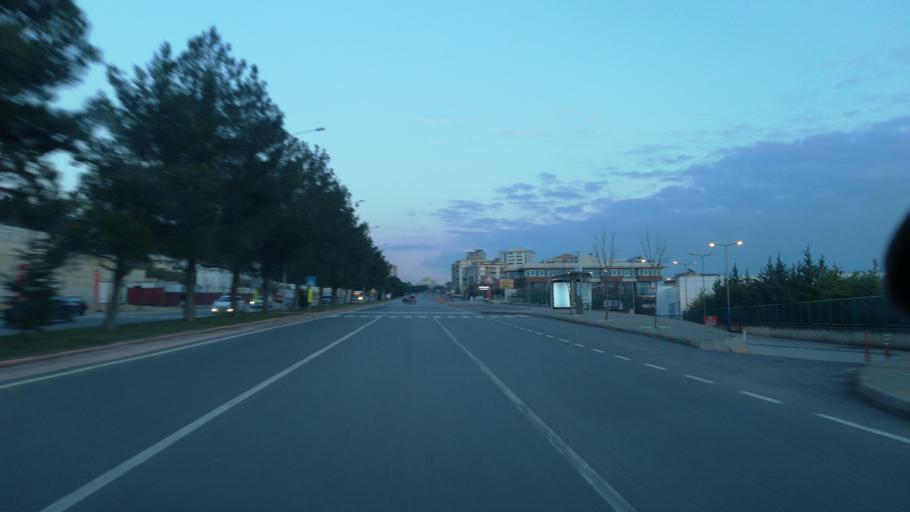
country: TR
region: Kahramanmaras
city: Kahramanmaras
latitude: 37.5991
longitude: 36.8390
